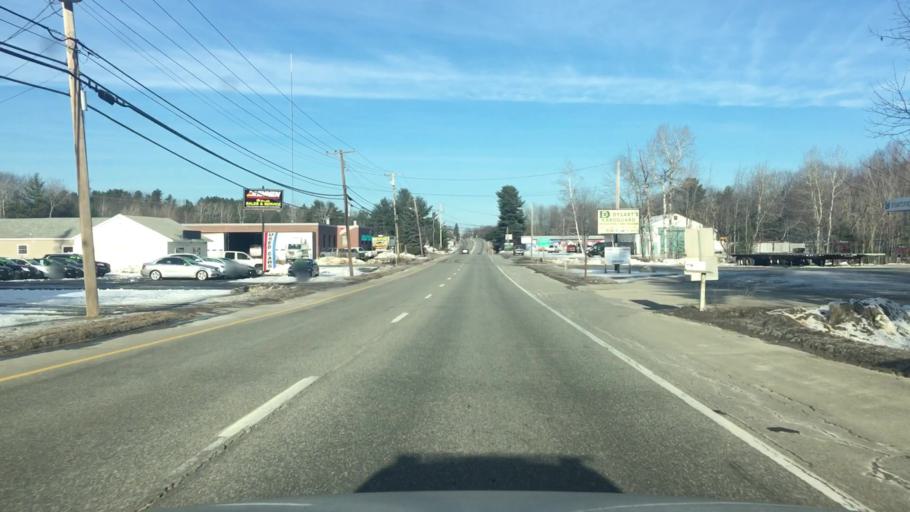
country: US
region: Maine
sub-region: Androscoggin County
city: Auburn
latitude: 44.0749
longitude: -70.2409
